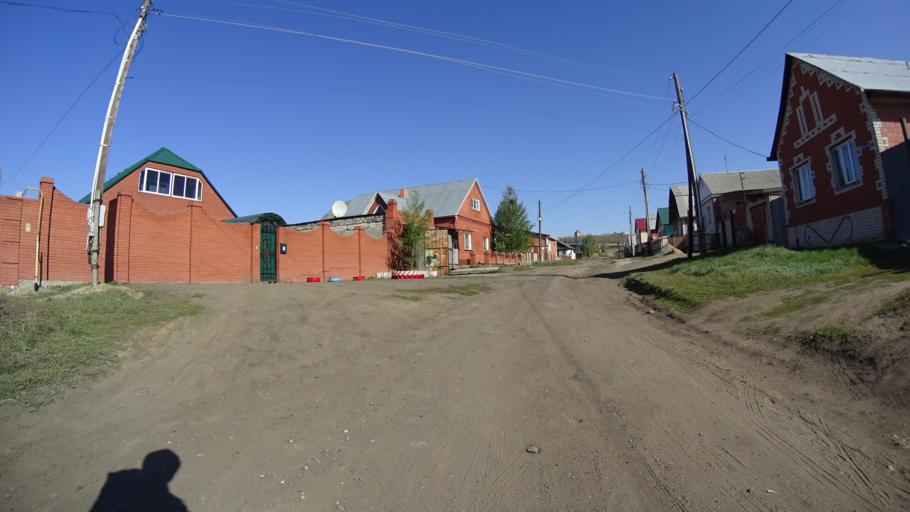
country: RU
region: Chelyabinsk
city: Troitsk
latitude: 54.0968
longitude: 61.5969
